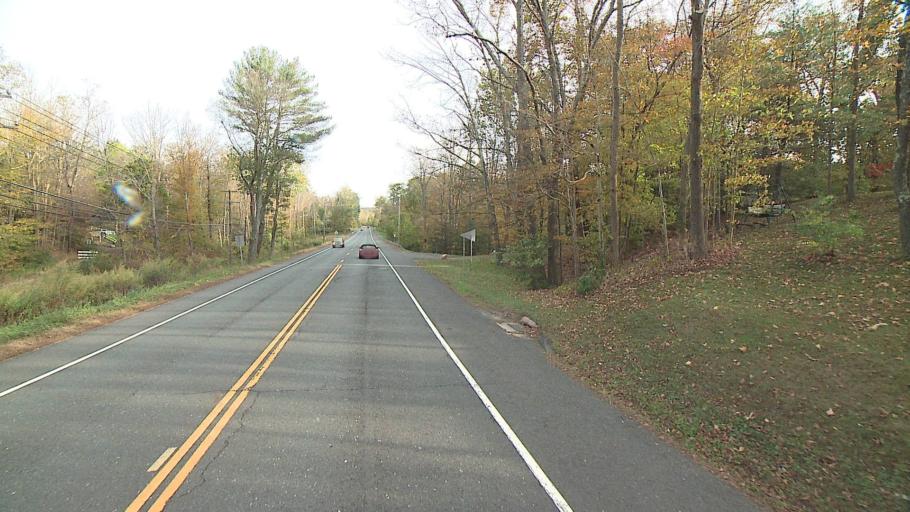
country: US
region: Connecticut
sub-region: Hartford County
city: Collinsville
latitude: 41.8447
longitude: -72.9416
